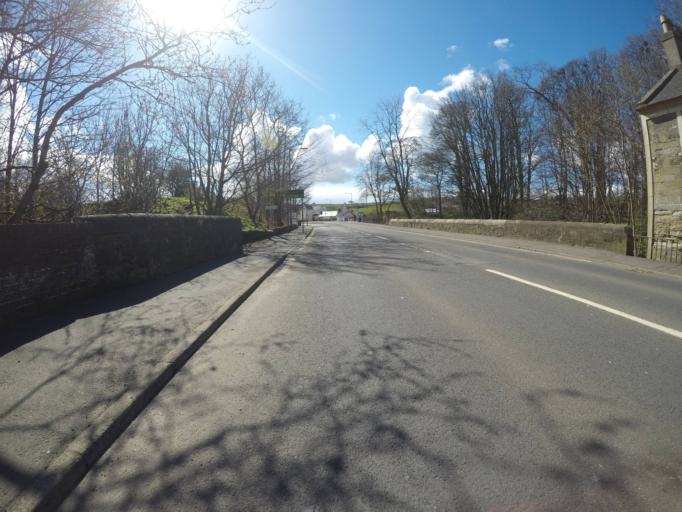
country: GB
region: Scotland
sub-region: North Ayrshire
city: Dalry
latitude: 55.7034
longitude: -4.7244
